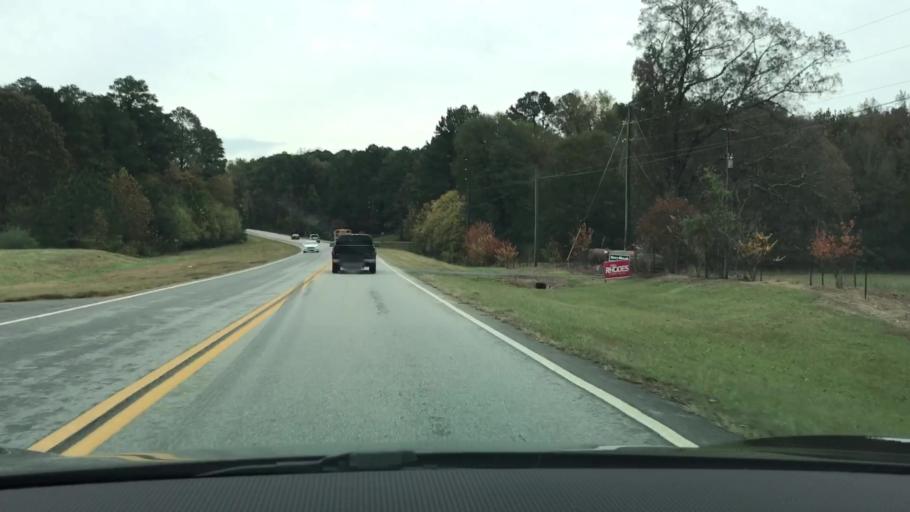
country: US
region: Georgia
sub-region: Greene County
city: Greensboro
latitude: 33.6425
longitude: -83.2285
